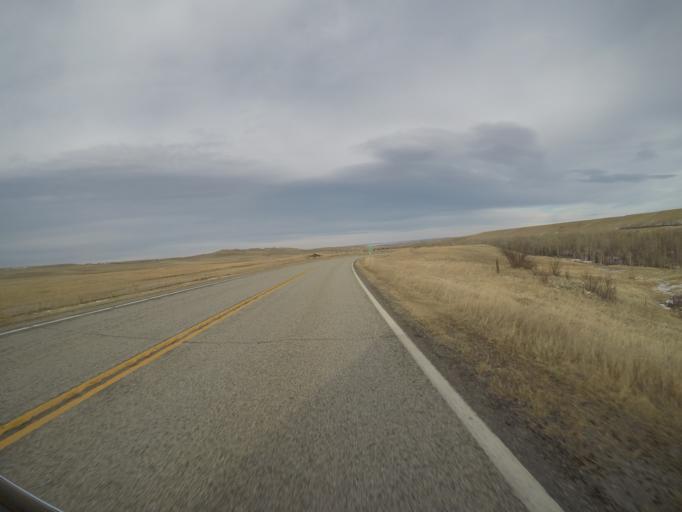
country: US
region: Montana
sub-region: Stillwater County
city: Absarokee
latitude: 45.4066
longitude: -109.4839
